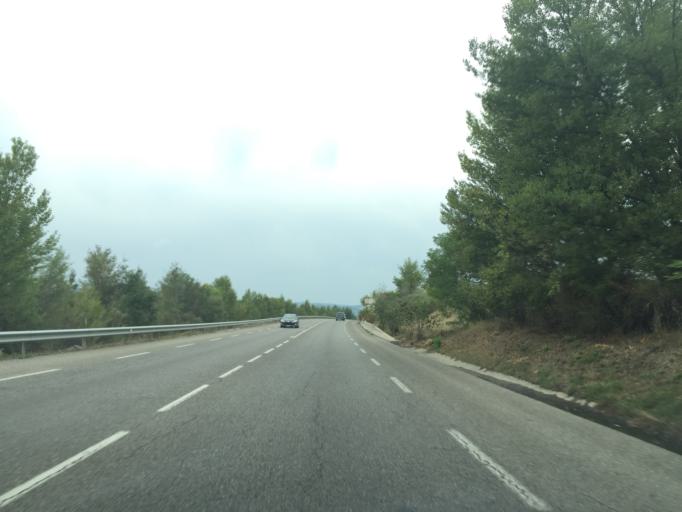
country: FR
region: Provence-Alpes-Cote d'Azur
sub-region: Departement des Alpes-de-Haute-Provence
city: Digne-les-Bains
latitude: 44.0721
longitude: 6.1843
